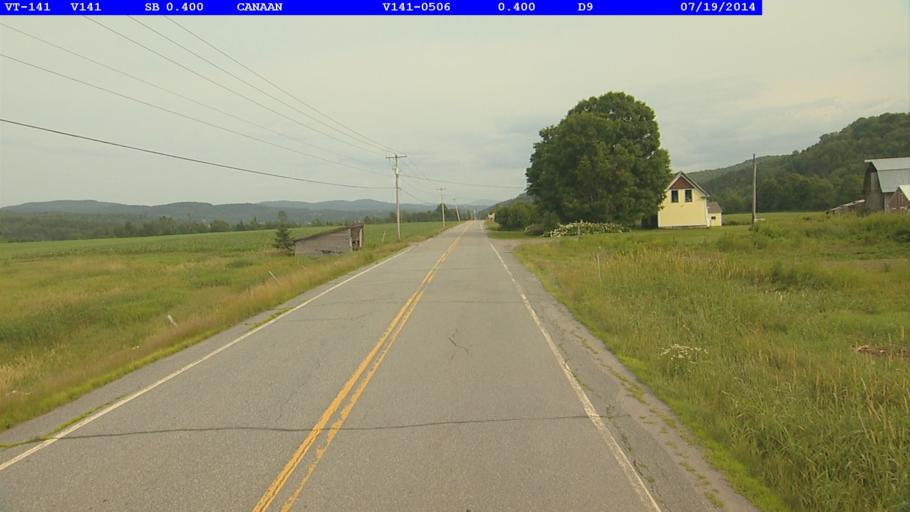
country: US
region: New Hampshire
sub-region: Coos County
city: Colebrook
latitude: 45.0116
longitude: -71.5595
